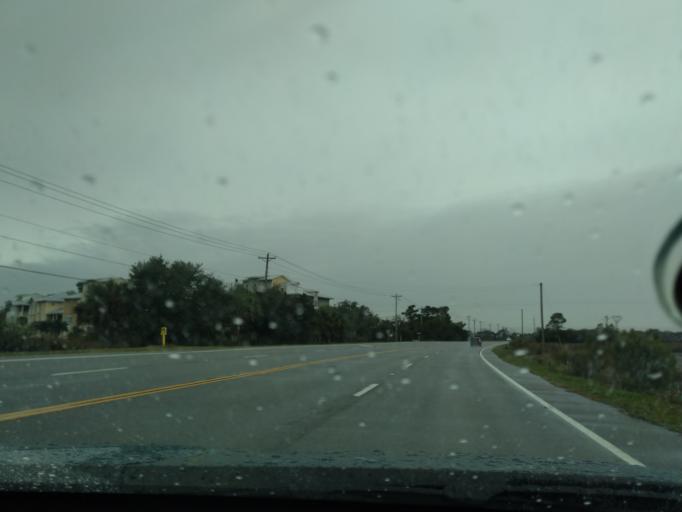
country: US
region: South Carolina
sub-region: Charleston County
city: Folly Beach
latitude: 32.6780
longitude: -79.9533
